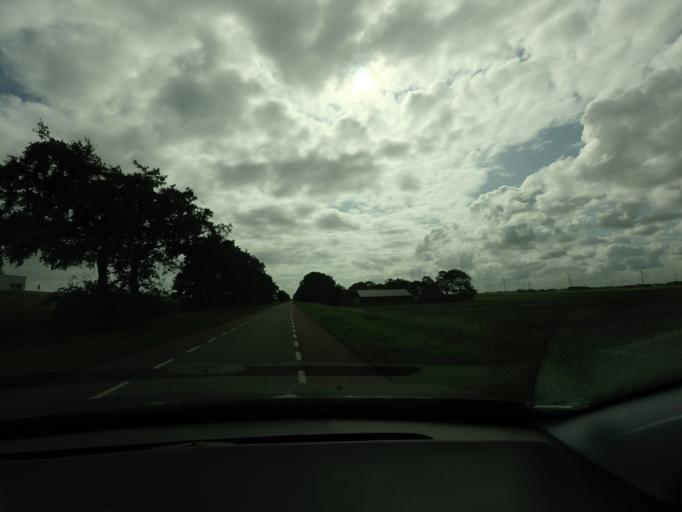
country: NL
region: North Holland
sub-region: Gemeente Medemblik
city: Medemblik
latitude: 52.8558
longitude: 5.1043
